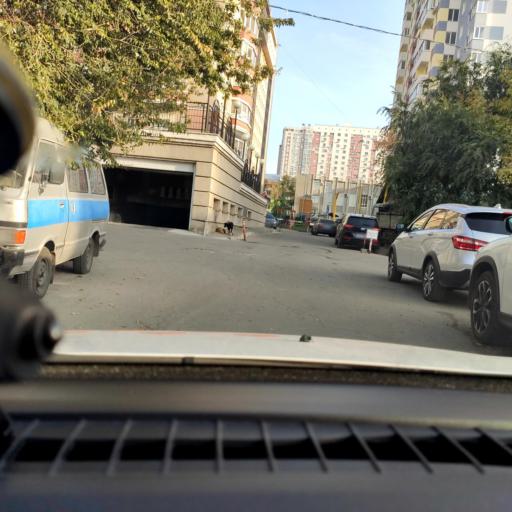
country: RU
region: Samara
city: Samara
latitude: 53.1878
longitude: 50.1317
